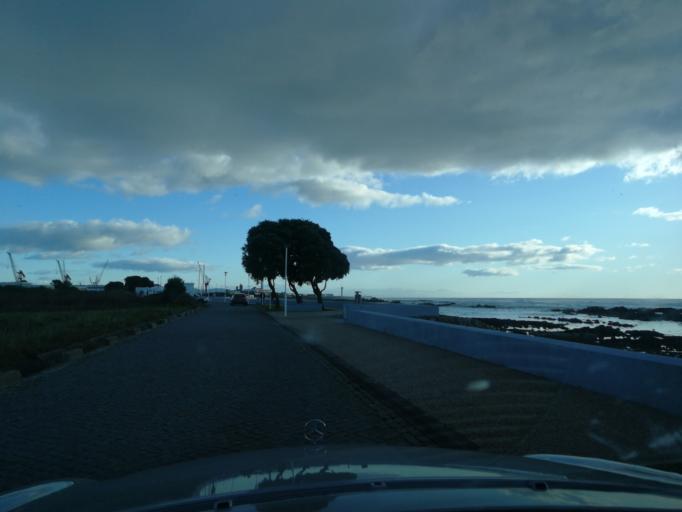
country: PT
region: Viana do Castelo
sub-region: Viana do Castelo
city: Areosa
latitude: 41.6989
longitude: -8.8525
